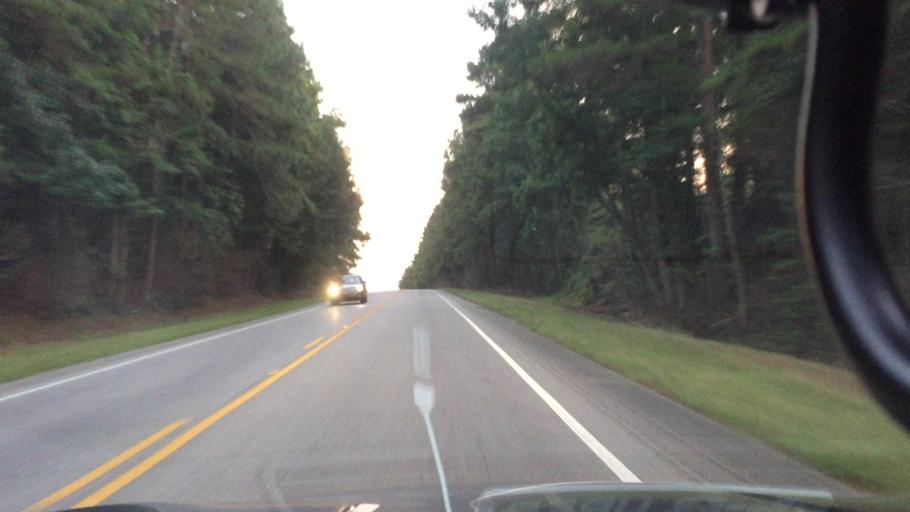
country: US
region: Alabama
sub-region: Coffee County
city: New Brockton
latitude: 31.3967
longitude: -85.8794
